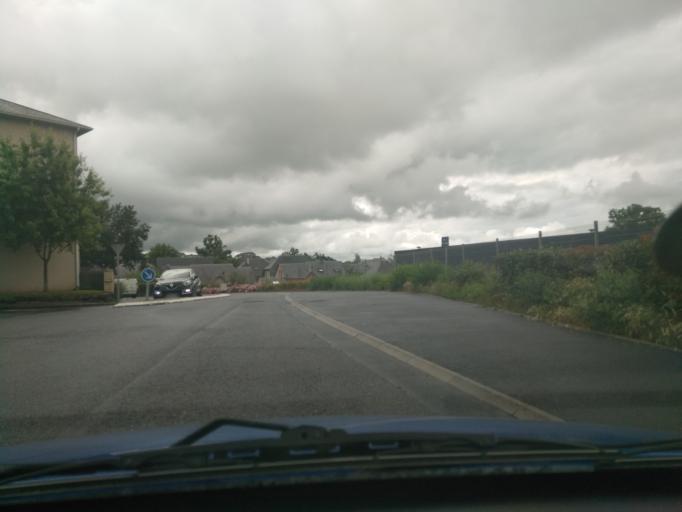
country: FR
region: Midi-Pyrenees
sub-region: Departement de l'Aveyron
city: Rodez
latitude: 44.3682
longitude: 2.5842
